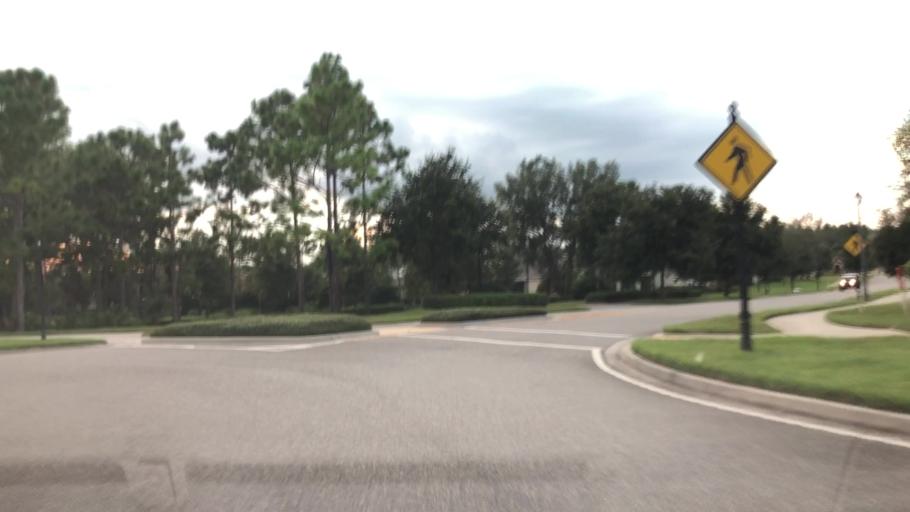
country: US
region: Florida
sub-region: Saint Johns County
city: Palm Valley
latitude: 30.1004
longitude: -81.4574
